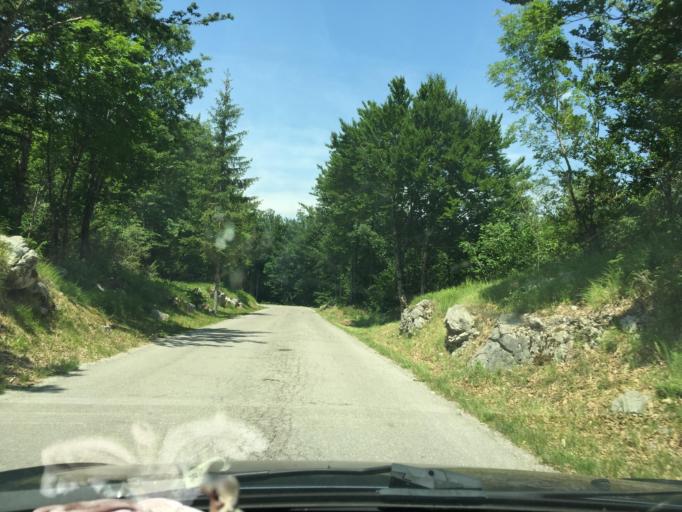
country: HR
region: Istarska
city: Buzet
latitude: 45.4585
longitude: 14.1406
